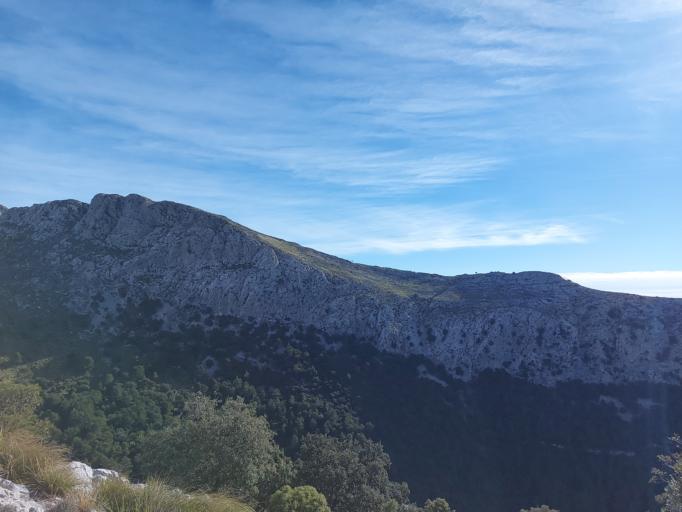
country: ES
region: Balearic Islands
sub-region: Illes Balears
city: Escorca
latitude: 39.7985
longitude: 2.8338
